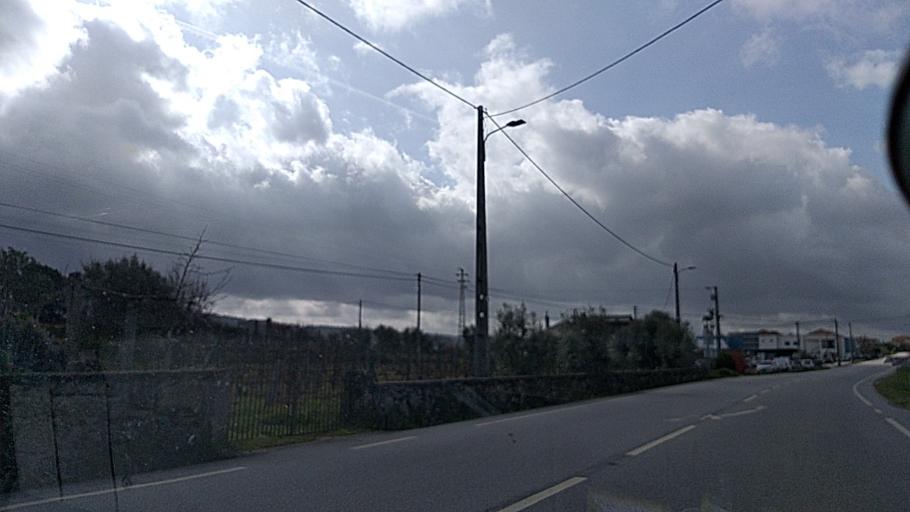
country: PT
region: Viseu
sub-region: Satao
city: Satao
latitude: 40.6671
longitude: -7.7123
